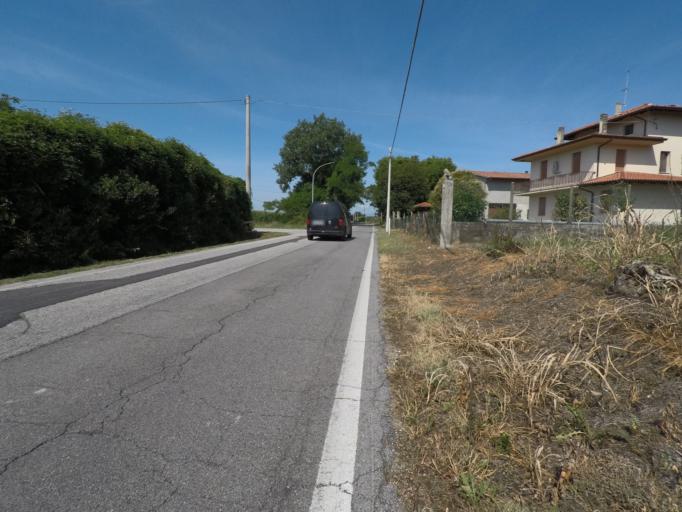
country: IT
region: Friuli Venezia Giulia
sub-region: Provincia di Udine
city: Coseano
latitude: 46.0713
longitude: 13.0184
